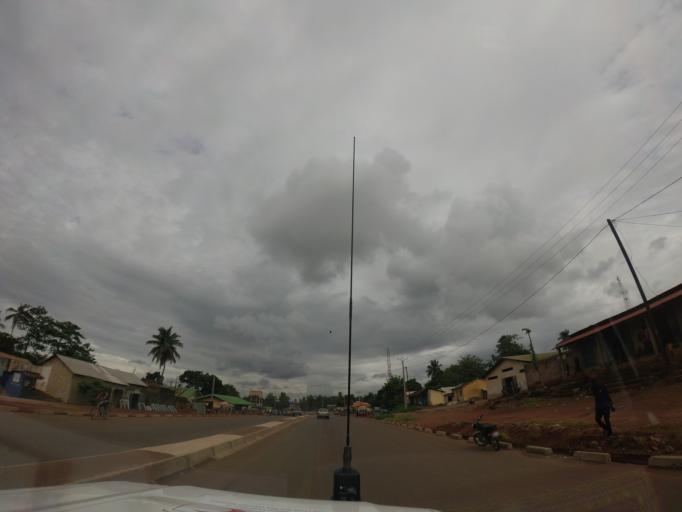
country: GN
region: Kindia
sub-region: Coyah
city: Coyah
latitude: 9.7074
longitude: -13.3915
